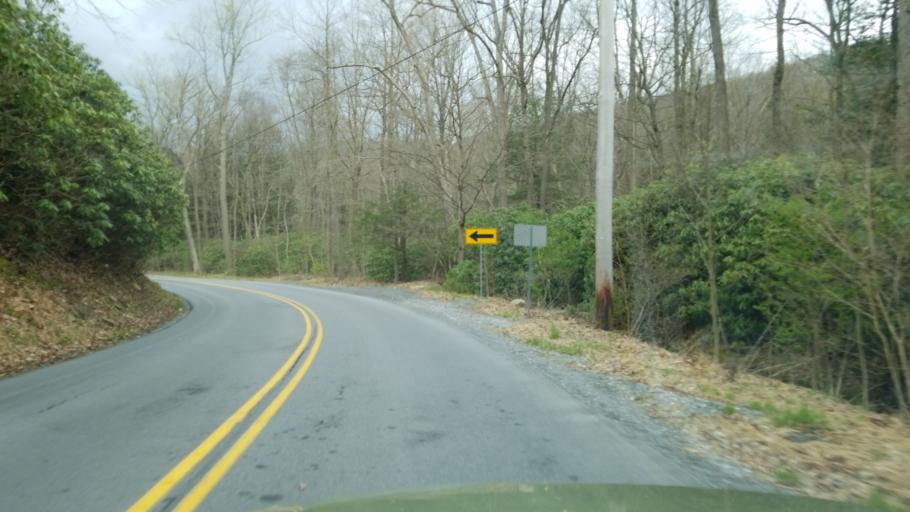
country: US
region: Pennsylvania
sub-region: Blair County
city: Tipton
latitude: 40.6692
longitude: -78.3298
